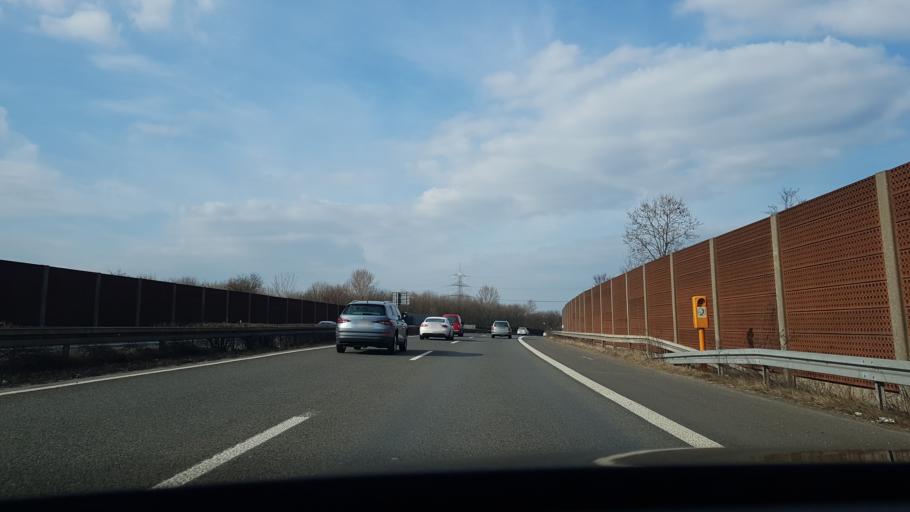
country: DE
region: North Rhine-Westphalia
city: Meiderich
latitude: 51.5107
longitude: 6.7585
